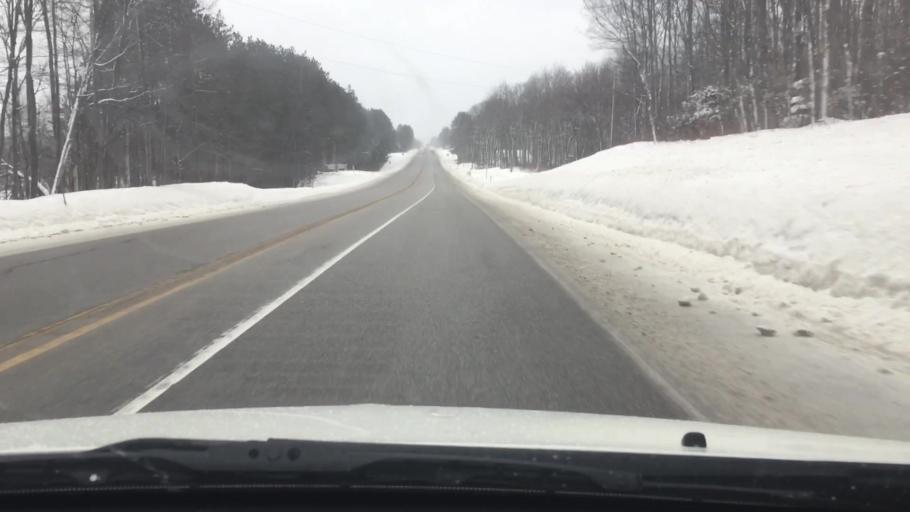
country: US
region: Michigan
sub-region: Otsego County
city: Gaylord
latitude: 45.0376
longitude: -84.7758
